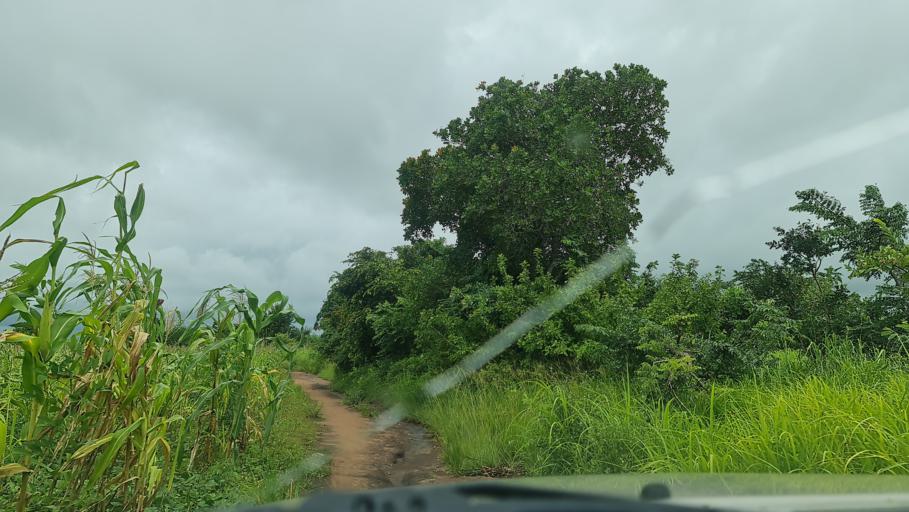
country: MW
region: Southern Region
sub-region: Nsanje District
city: Nsanje
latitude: -17.3910
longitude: 35.7819
